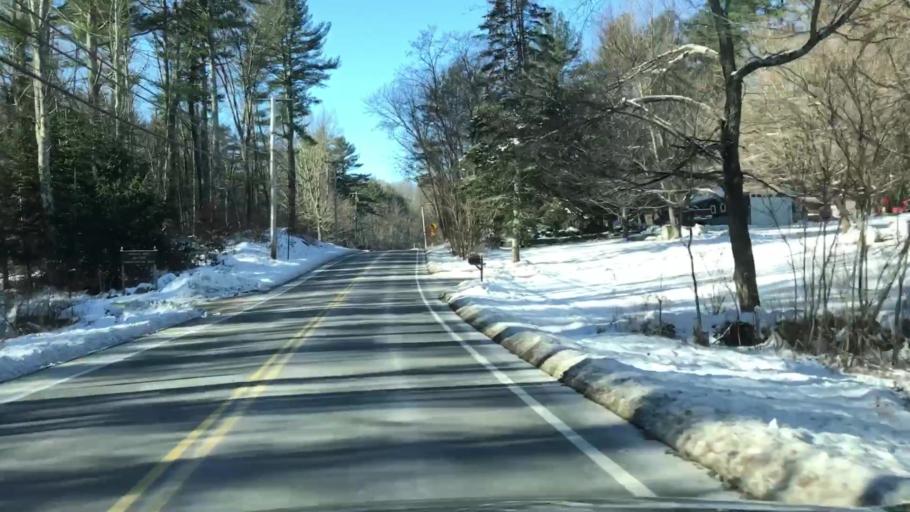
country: US
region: New Hampshire
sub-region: Hillsborough County
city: Bedford
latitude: 42.9426
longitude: -71.5346
